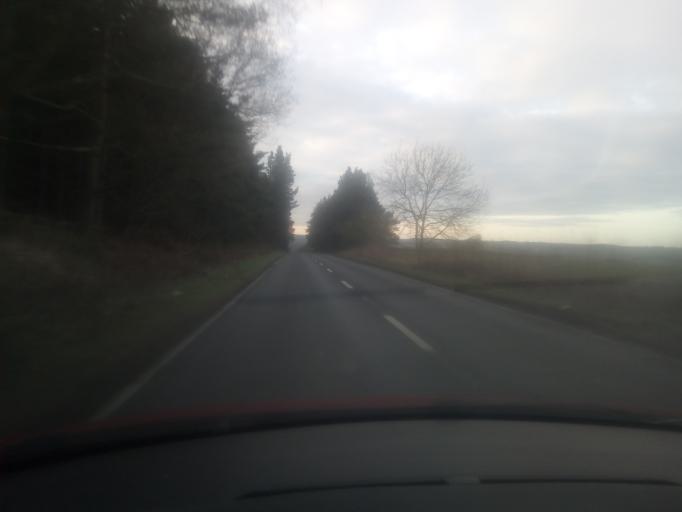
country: GB
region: England
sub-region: Northumberland
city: Healey
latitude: 54.9279
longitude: -1.9618
